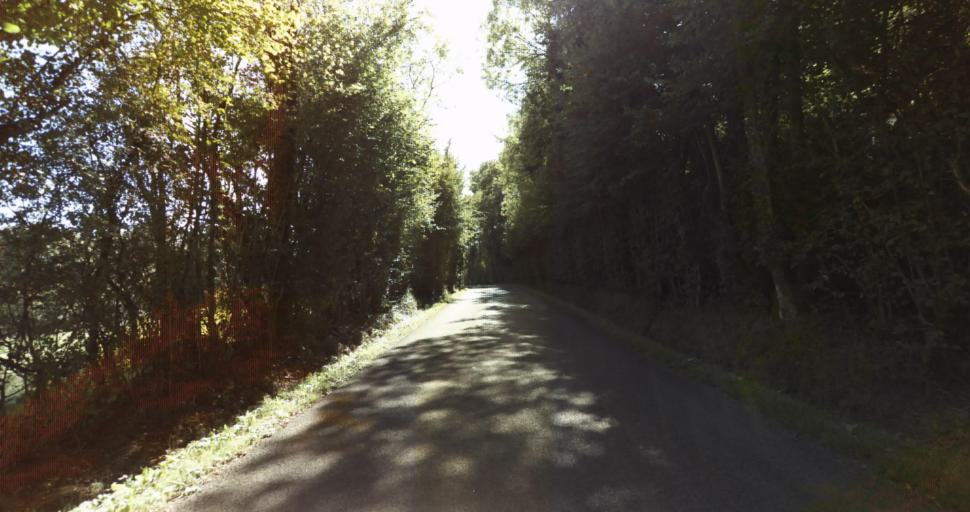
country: FR
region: Lower Normandy
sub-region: Departement de l'Orne
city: Gace
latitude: 48.7643
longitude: 0.2539
